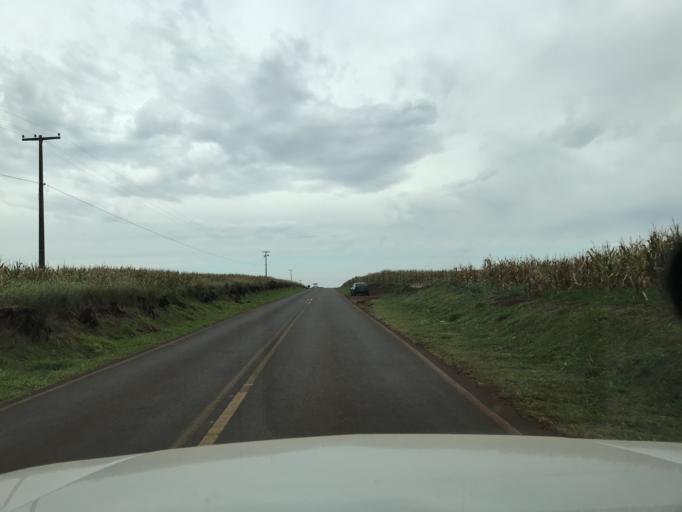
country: BR
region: Parana
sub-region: Marechal Candido Rondon
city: Marechal Candido Rondon
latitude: -24.4512
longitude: -53.9279
